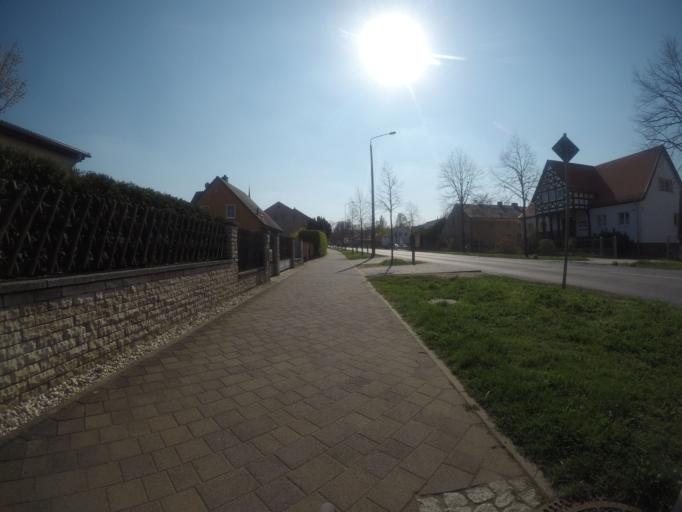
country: DE
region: Brandenburg
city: Potsdam
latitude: 52.4260
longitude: 13.0013
